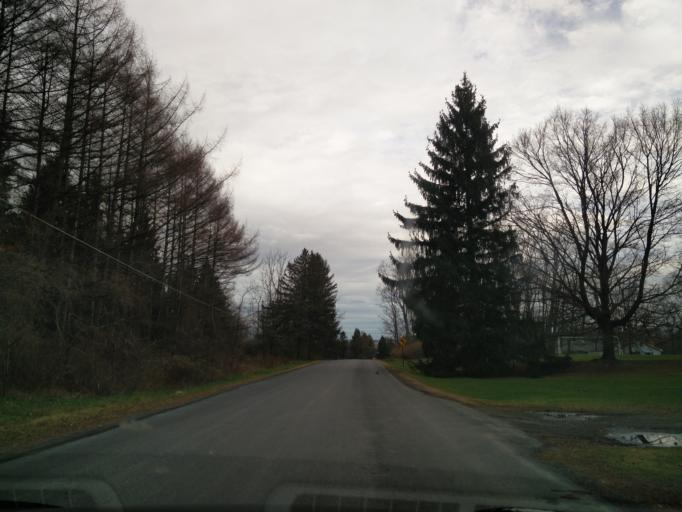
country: US
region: New York
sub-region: Tompkins County
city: Trumansburg
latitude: 42.5263
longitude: -76.6809
